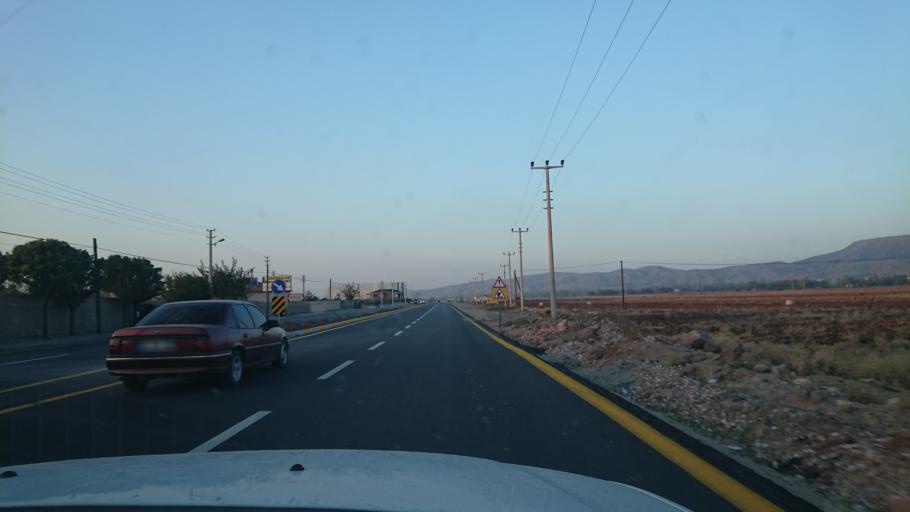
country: TR
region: Aksaray
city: Aksaray
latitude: 38.3197
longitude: 34.0531
